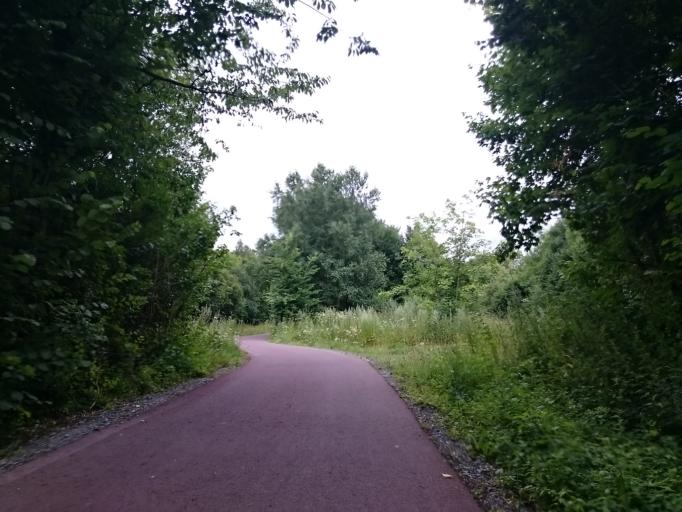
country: FR
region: Lower Normandy
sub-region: Departement du Calvados
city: Saint-Andre-sur-Orne
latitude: 49.1134
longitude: -0.3886
